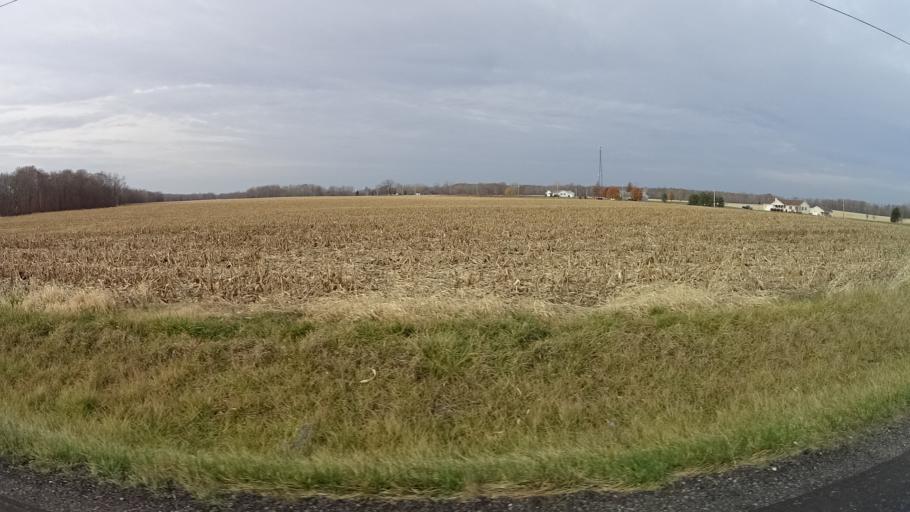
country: US
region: Ohio
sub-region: Lorain County
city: Lagrange
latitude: 41.1528
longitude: -82.1234
